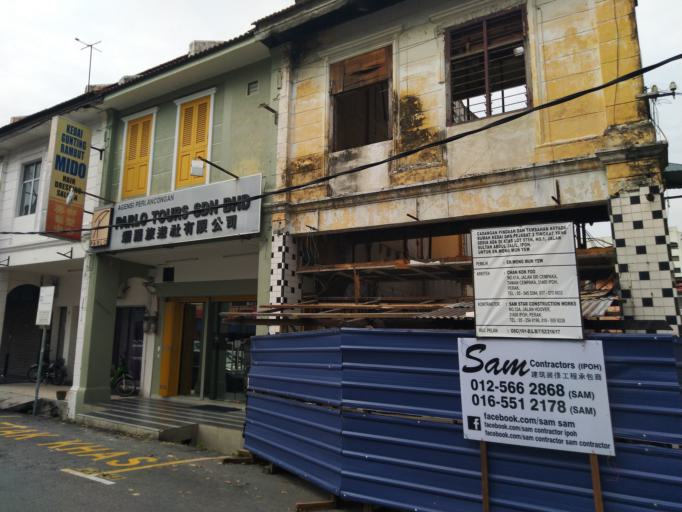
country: MY
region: Perak
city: Ipoh
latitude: 4.5981
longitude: 101.0848
